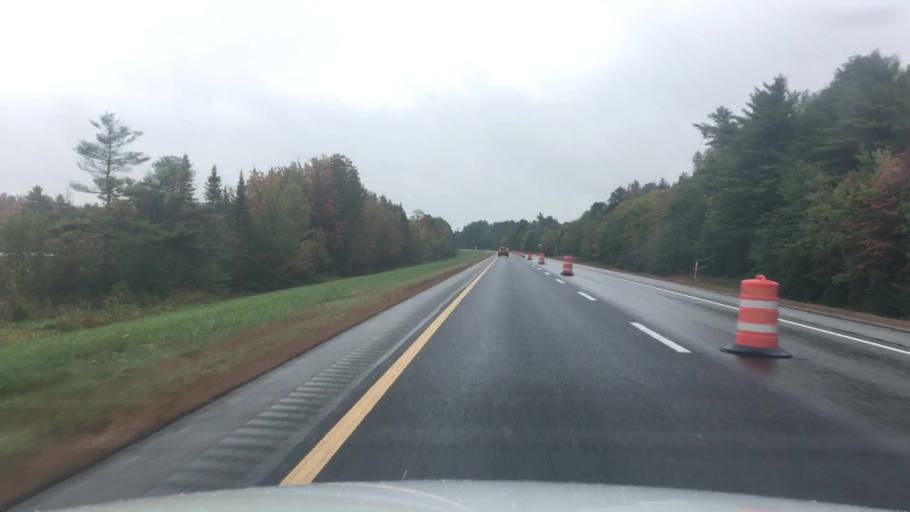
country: US
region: Maine
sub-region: Sagadahoc County
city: Richmond
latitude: 44.1171
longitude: -69.8544
